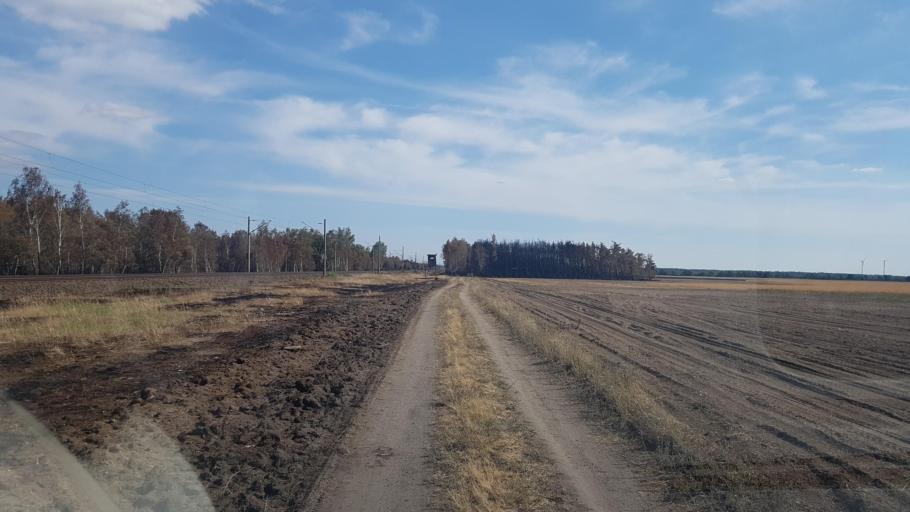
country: DE
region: Brandenburg
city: Muhlberg
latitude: 51.4324
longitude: 13.3043
